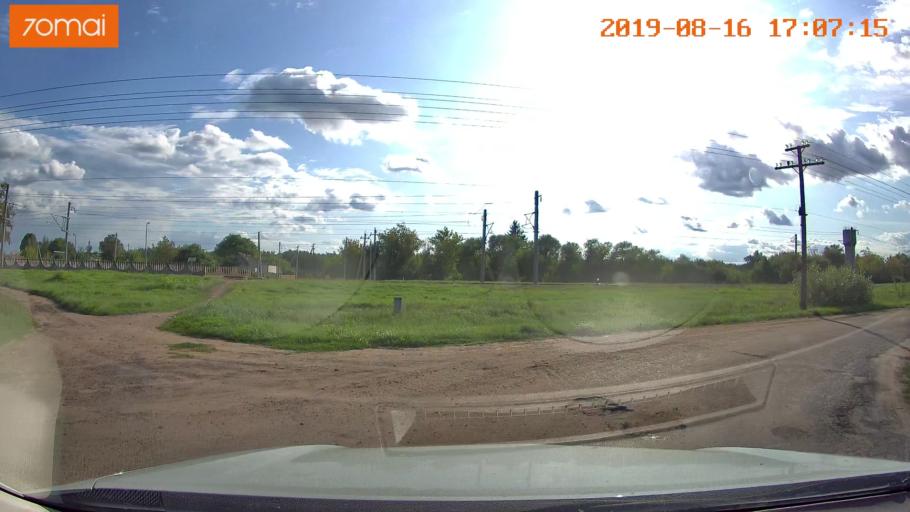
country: BY
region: Mogilev
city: Hlusha
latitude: 53.2207
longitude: 28.9260
